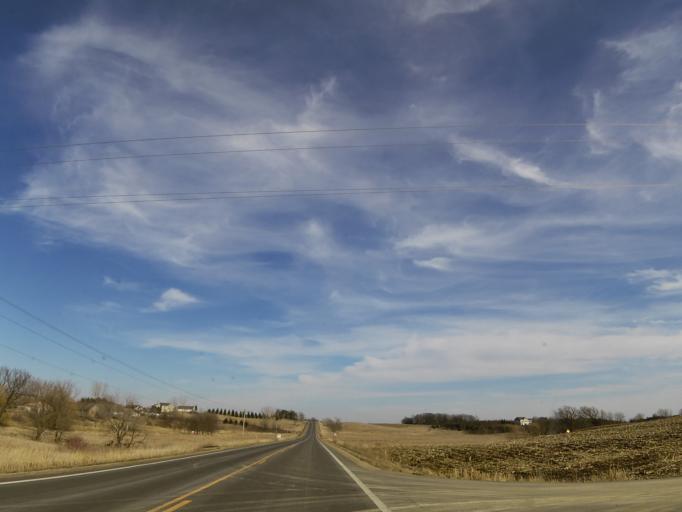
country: US
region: Minnesota
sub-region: Scott County
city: Elko New Market
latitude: 44.5440
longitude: -93.3361
